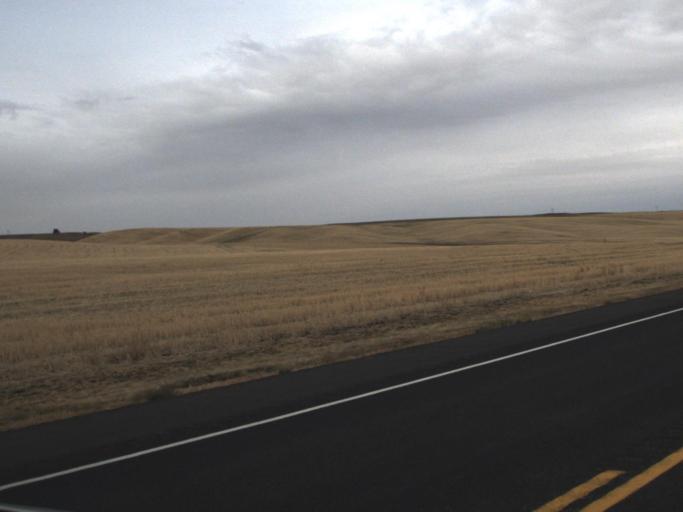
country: US
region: Washington
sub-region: Asotin County
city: Clarkston
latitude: 46.4910
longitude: -117.0732
